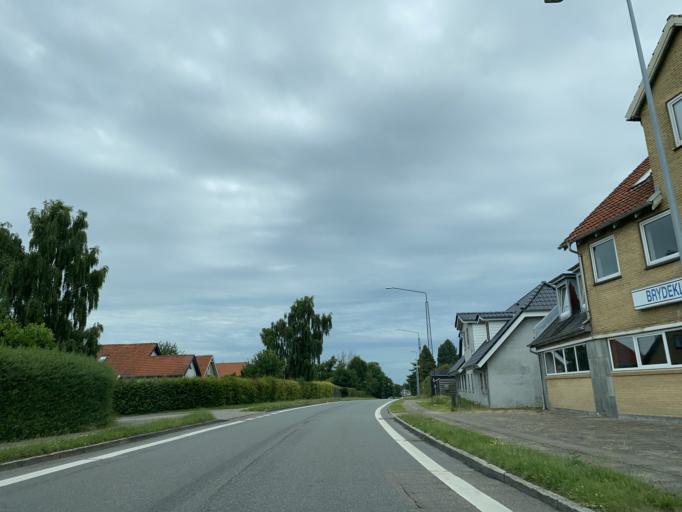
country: DK
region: South Denmark
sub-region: Sonderborg Kommune
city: Sonderborg
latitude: 54.9204
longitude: 9.7981
